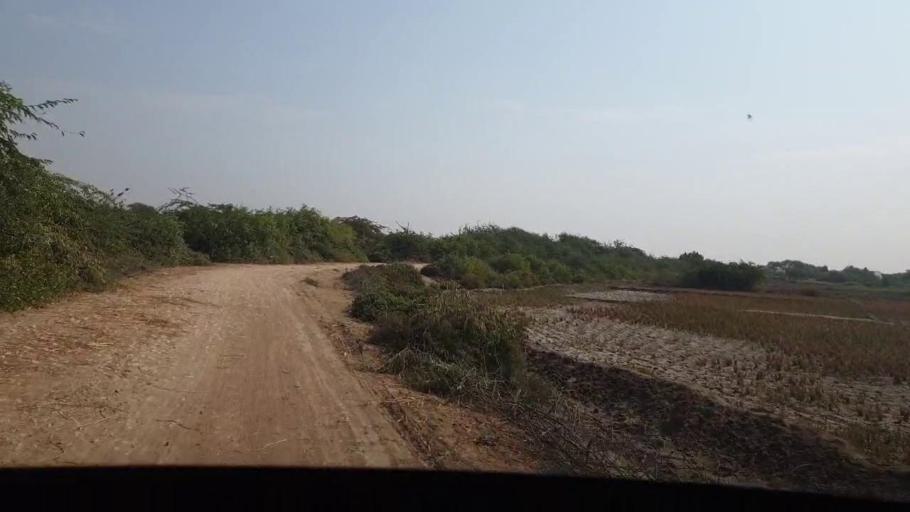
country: PK
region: Sindh
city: Chuhar Jamali
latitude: 24.2690
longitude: 67.9230
